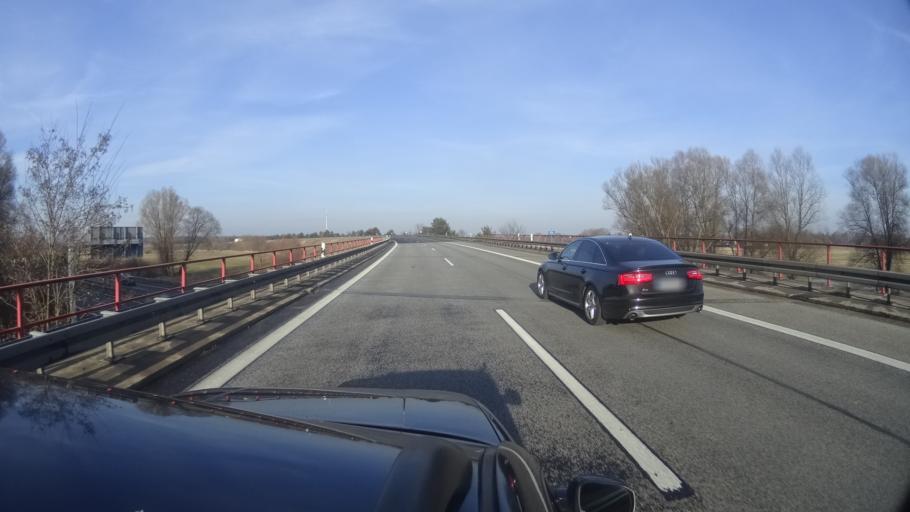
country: DE
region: Brandenburg
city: Leegebruch
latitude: 52.7051
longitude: 13.1949
